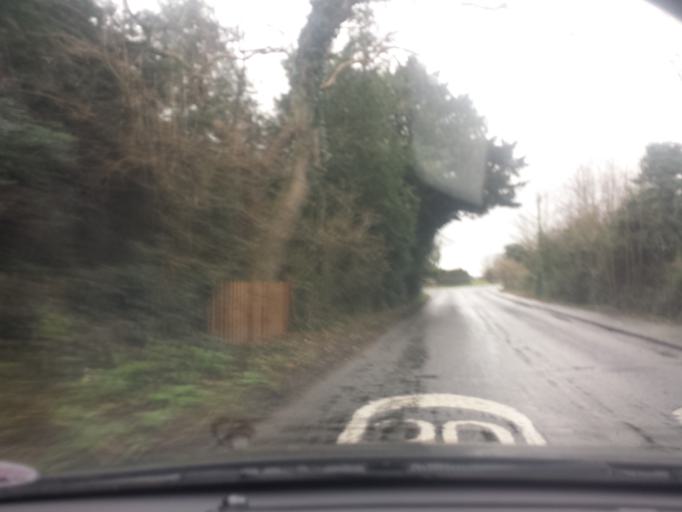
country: GB
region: England
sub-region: Essex
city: Great Bentley
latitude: 51.8757
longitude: 1.1118
